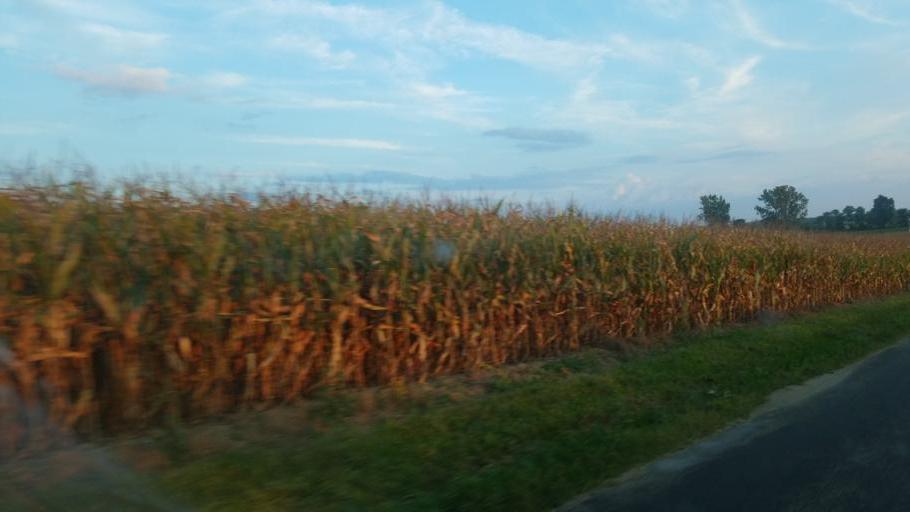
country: US
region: Ohio
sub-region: Knox County
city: Fredericktown
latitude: 40.4459
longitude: -82.5676
